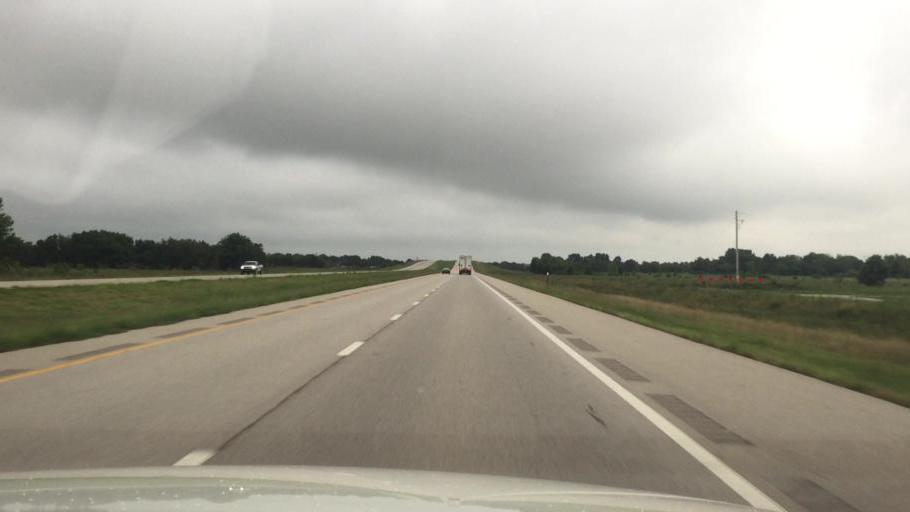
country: US
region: Kansas
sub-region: Montgomery County
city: Coffeyville
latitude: 37.0945
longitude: -95.5898
